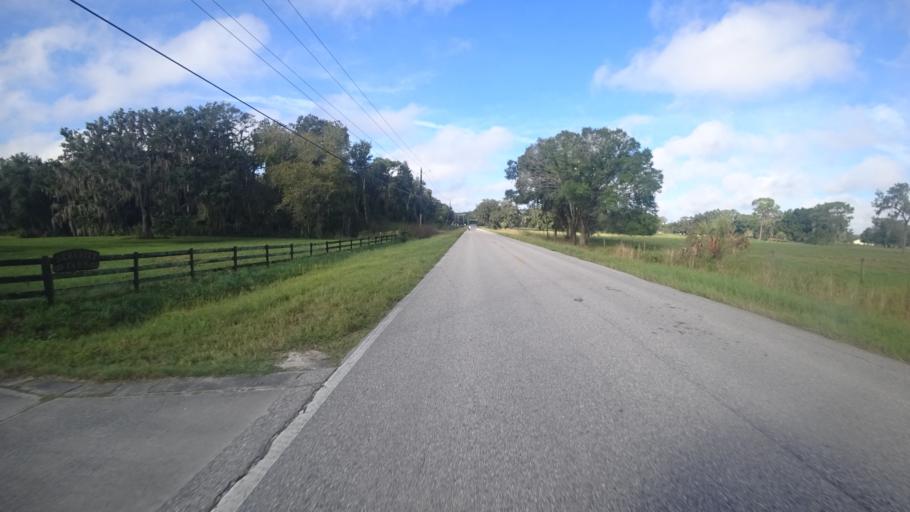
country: US
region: Florida
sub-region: Manatee County
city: Ellenton
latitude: 27.5575
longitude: -82.4220
